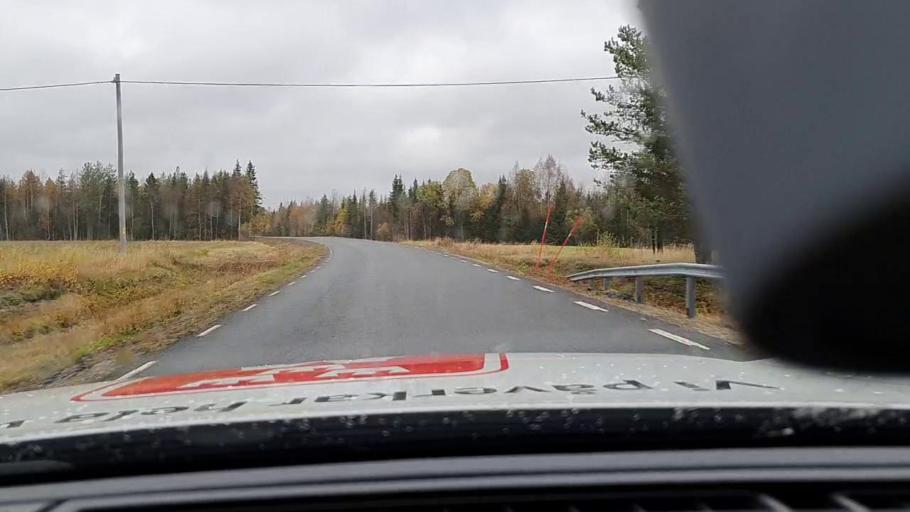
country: SE
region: Norrbotten
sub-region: Haparanda Kommun
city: Haparanda
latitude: 65.9334
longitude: 23.8146
